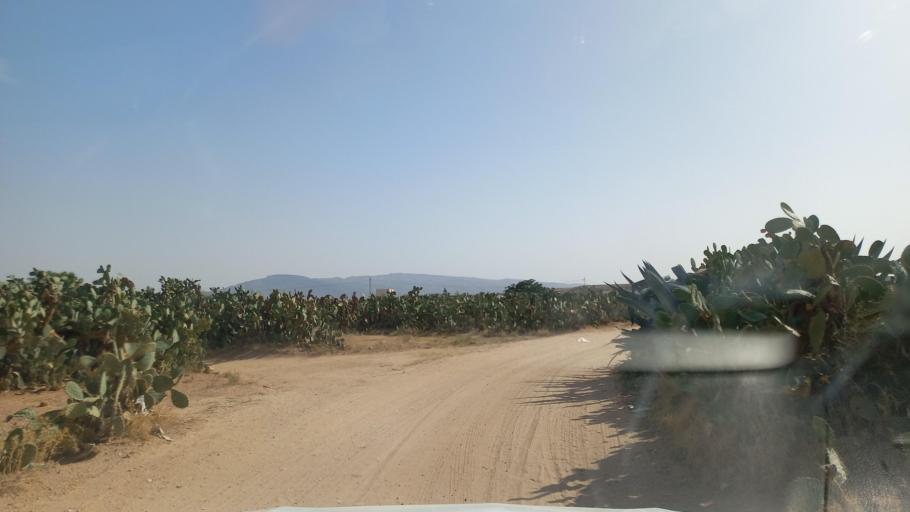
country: TN
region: Al Qasrayn
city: Kasserine
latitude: 35.2735
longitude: 8.9408
